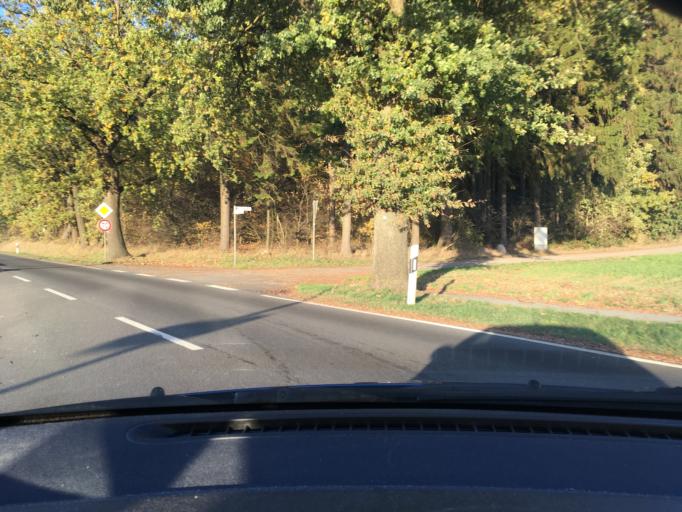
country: DE
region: Lower Saxony
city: Buchholz in der Nordheide
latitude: 53.3578
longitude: 9.8751
